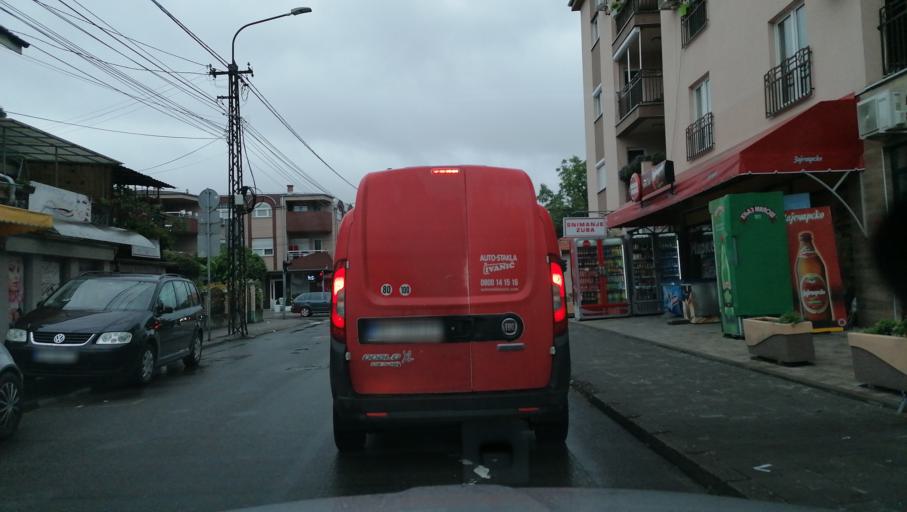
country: RS
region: Central Serbia
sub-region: Rasinski Okrug
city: Krusevac
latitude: 43.5822
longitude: 21.3208
